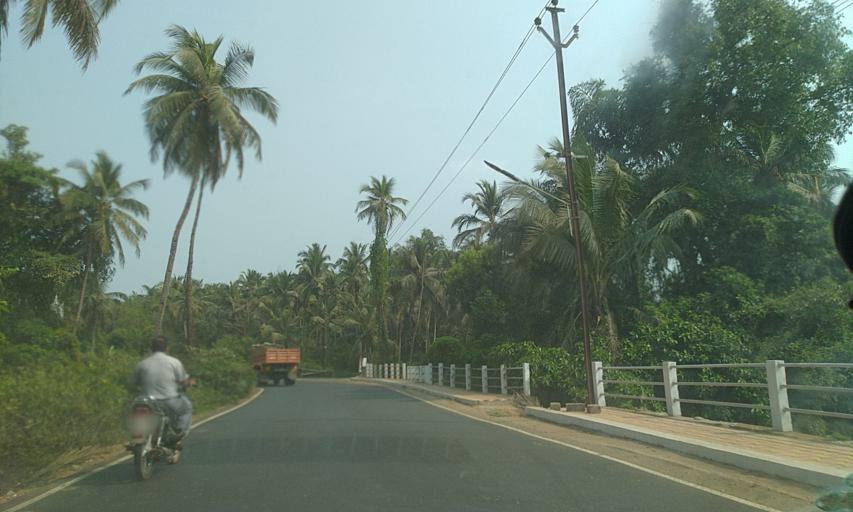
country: IN
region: Goa
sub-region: South Goa
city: Quepem
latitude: 15.2560
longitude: 74.0501
